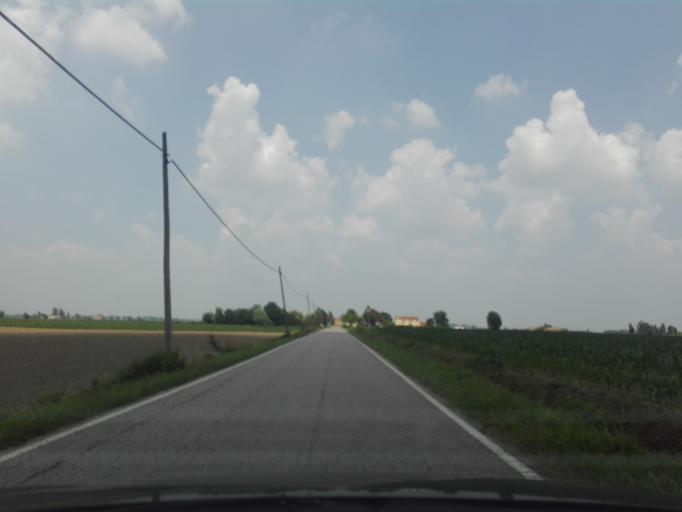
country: IT
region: Veneto
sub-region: Provincia di Rovigo
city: Crespino
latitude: 45.0005
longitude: 11.9006
